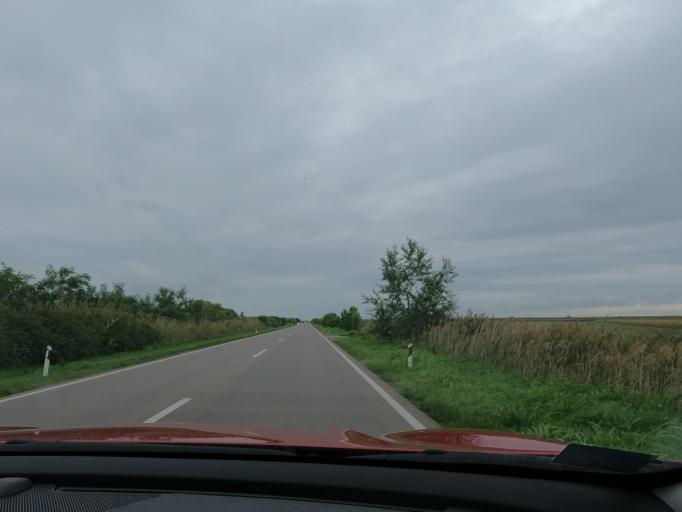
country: RS
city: Basaid
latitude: 45.6586
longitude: 20.4207
